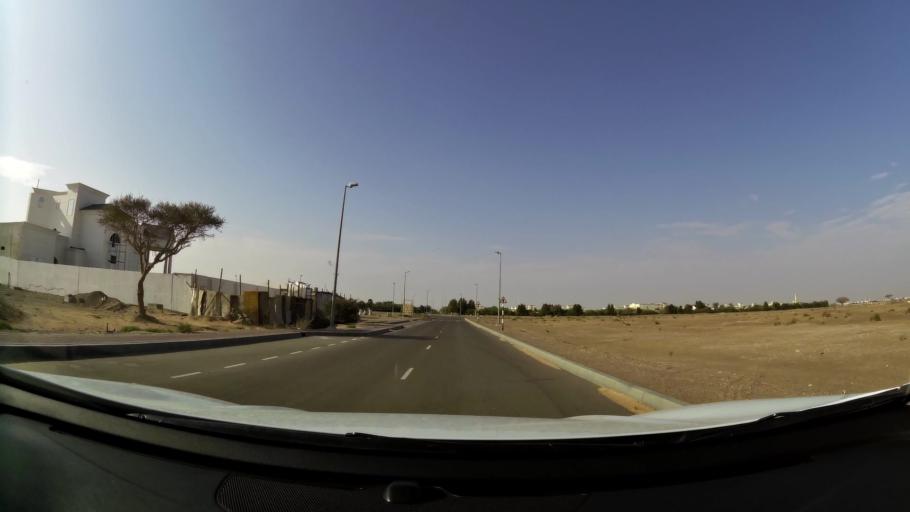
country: AE
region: Abu Dhabi
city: Al Ain
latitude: 24.0534
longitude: 55.8496
